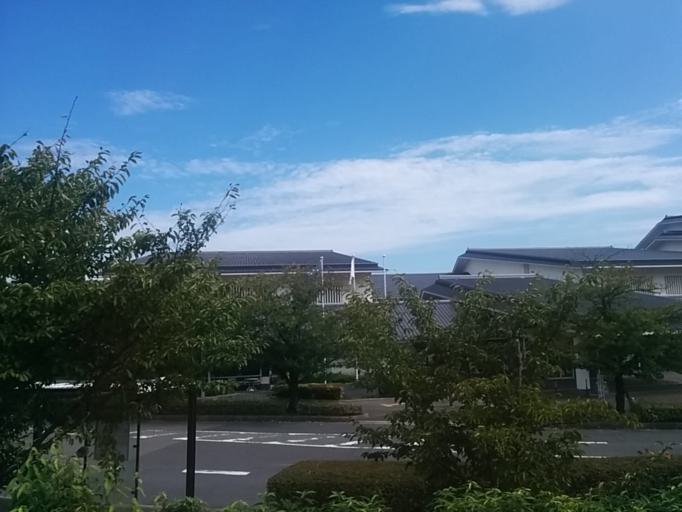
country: JP
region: Nara
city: Nara-shi
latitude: 34.6524
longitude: 135.7817
